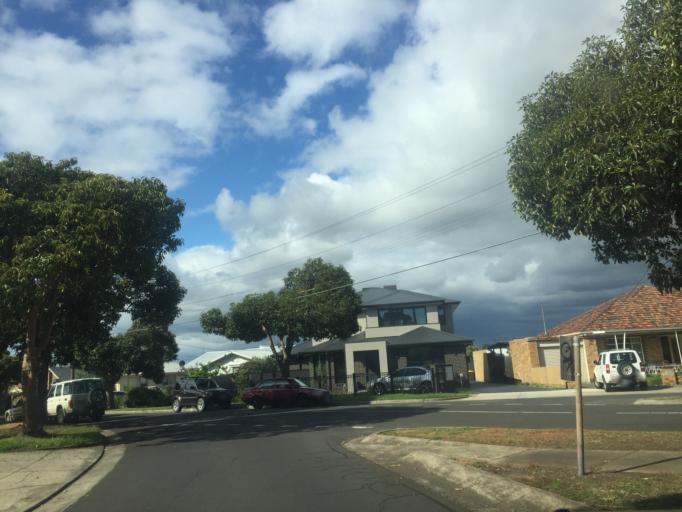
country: AU
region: Victoria
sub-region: Darebin
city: Kingsbury
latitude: -37.7247
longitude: 145.0189
